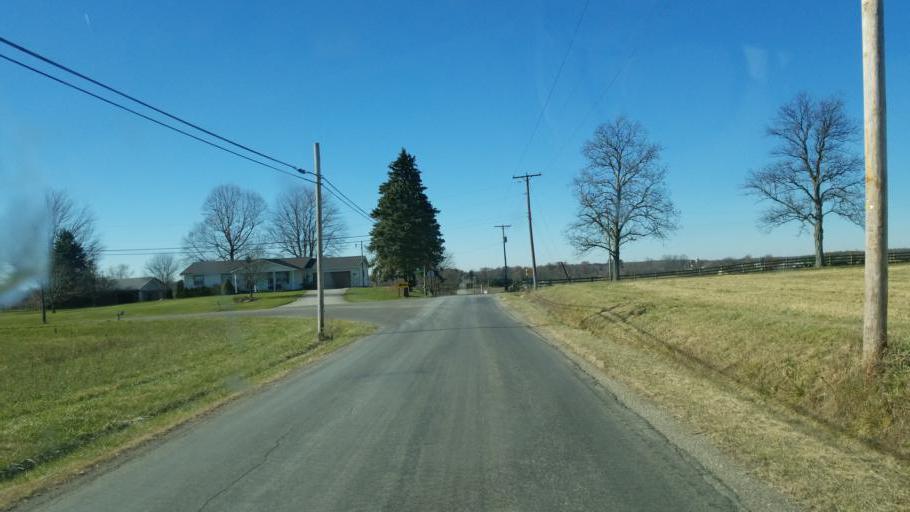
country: US
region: Ohio
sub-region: Huron County
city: Plymouth
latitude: 40.9746
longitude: -82.5906
